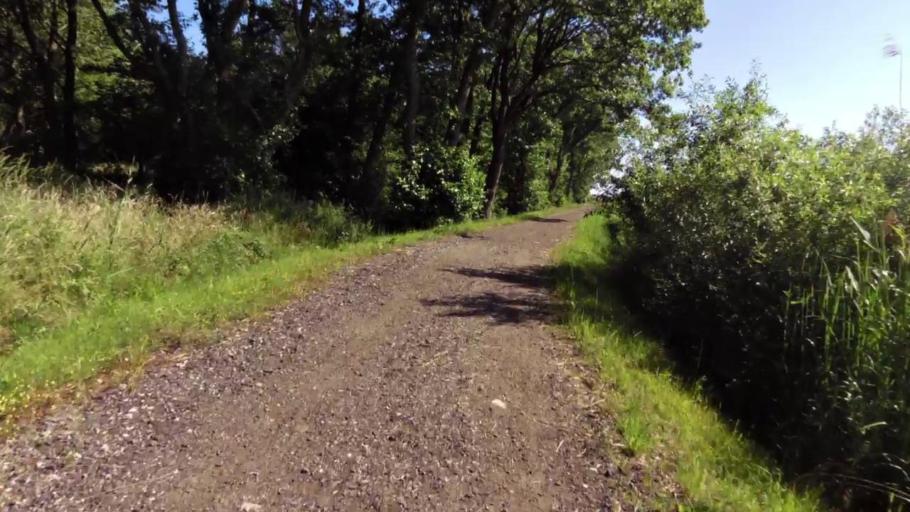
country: PL
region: West Pomeranian Voivodeship
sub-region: Powiat koszalinski
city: Mielno
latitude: 54.2700
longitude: 16.1100
